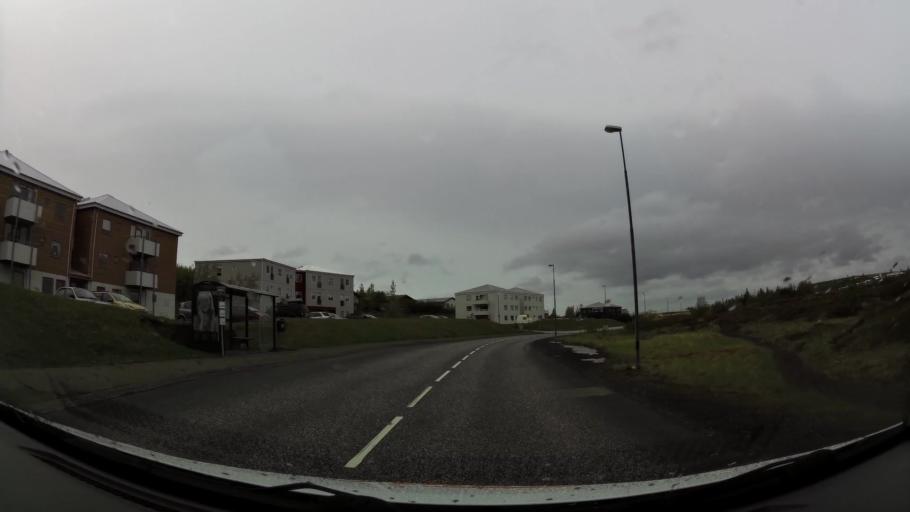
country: IS
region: Capital Region
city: Hafnarfjoerdur
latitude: 64.0604
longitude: -21.9328
